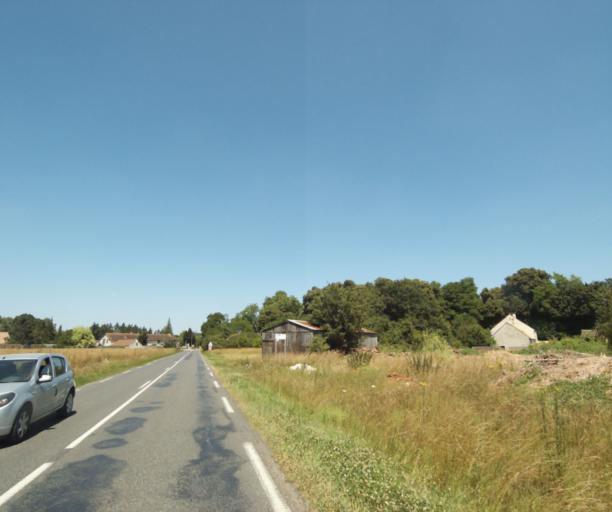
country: FR
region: Ile-de-France
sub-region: Departement de l'Essonne
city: Milly-la-Foret
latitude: 48.3777
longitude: 2.4759
